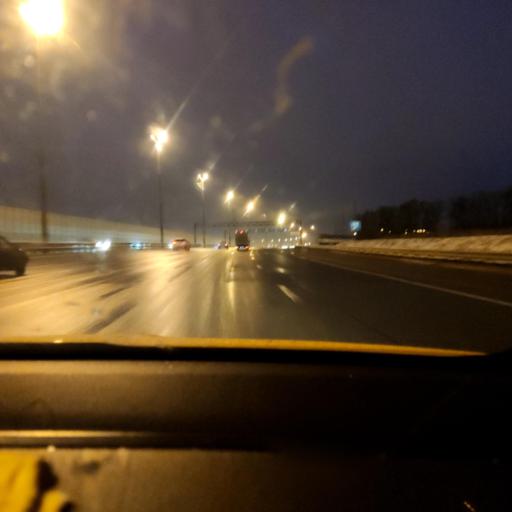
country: RU
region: Moskovskaya
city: Bolshevo
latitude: 55.9495
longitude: 37.8185
